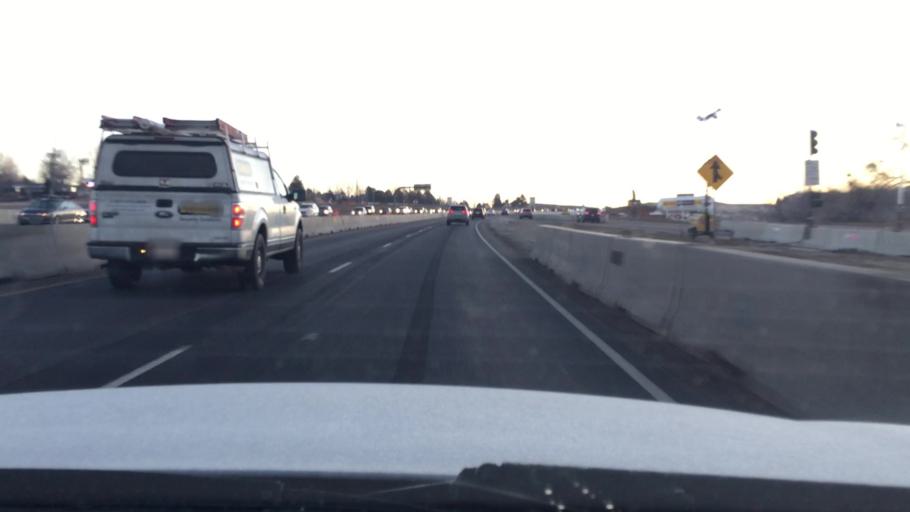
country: US
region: Colorado
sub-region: Douglas County
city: Highlands Ranch
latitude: 39.5649
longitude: -104.9848
